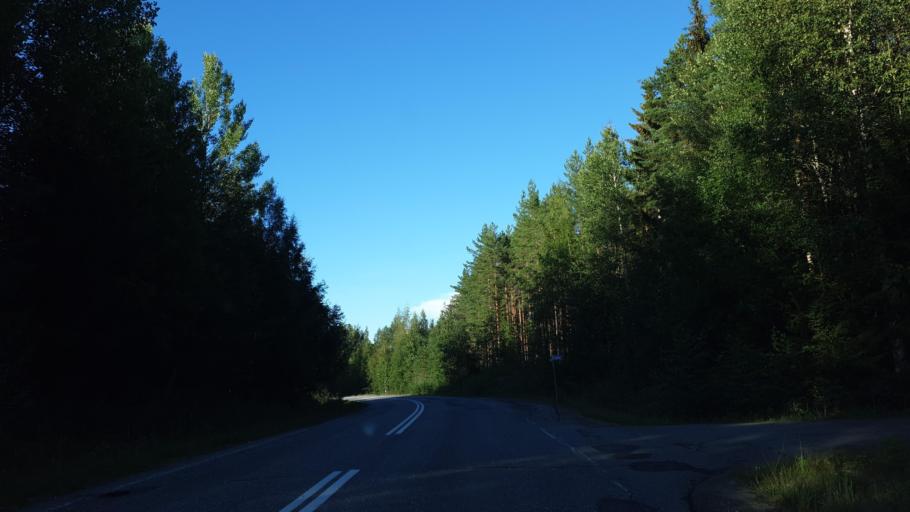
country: FI
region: Northern Savo
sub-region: Koillis-Savo
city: Juankoski
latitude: 63.0570
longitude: 28.3917
